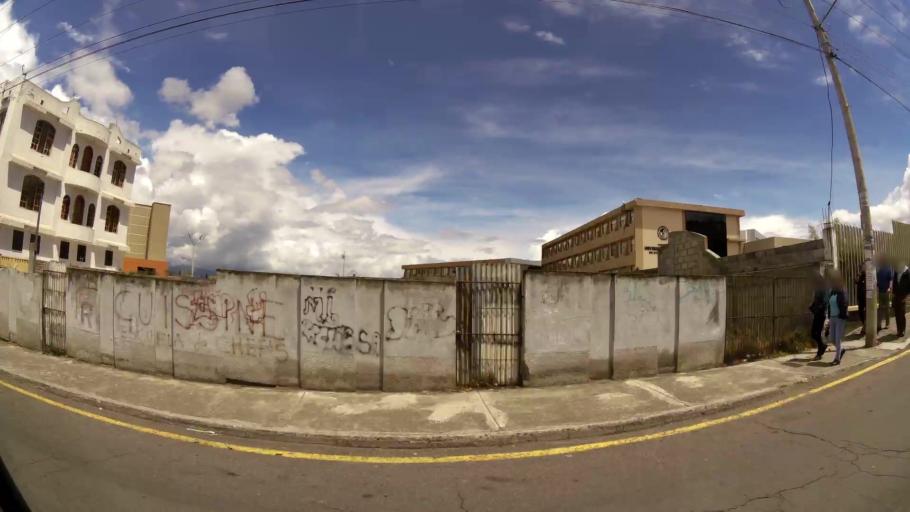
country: EC
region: Tungurahua
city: Ambato
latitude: -1.2739
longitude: -78.6392
